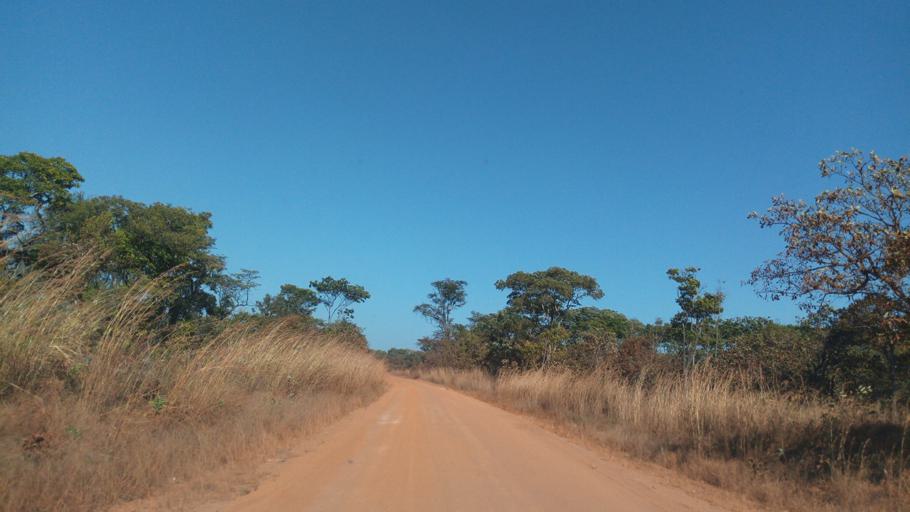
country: ZM
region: Luapula
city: Mwense
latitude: -10.6847
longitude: 28.3974
